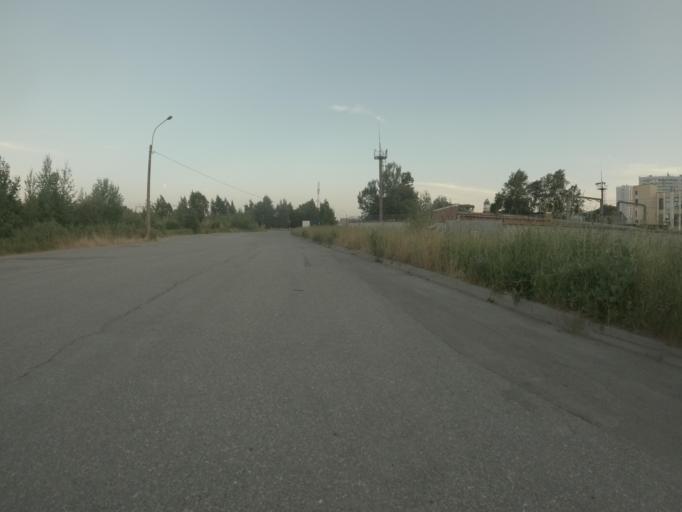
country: RU
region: St.-Petersburg
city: Krasnogvargeisky
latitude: 59.9385
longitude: 30.4462
